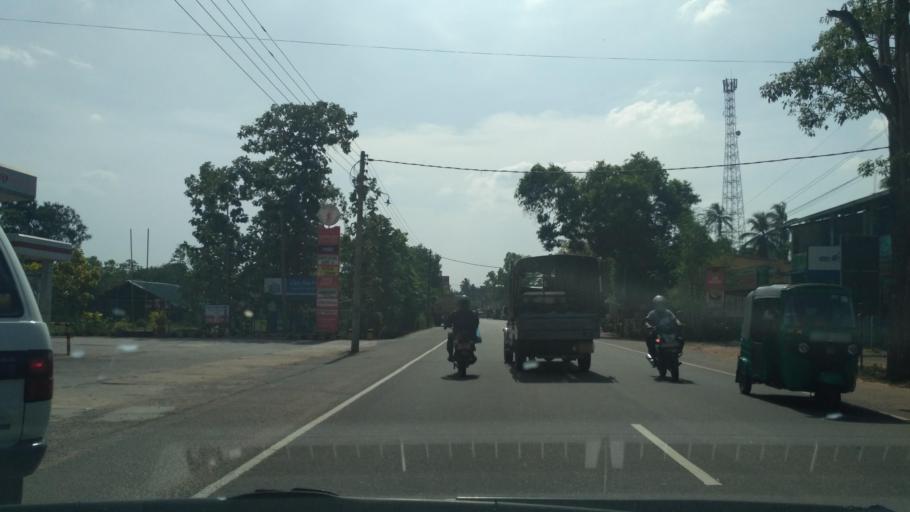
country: LK
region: North Western
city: Kuliyapitiya
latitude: 7.3307
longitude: 80.0266
